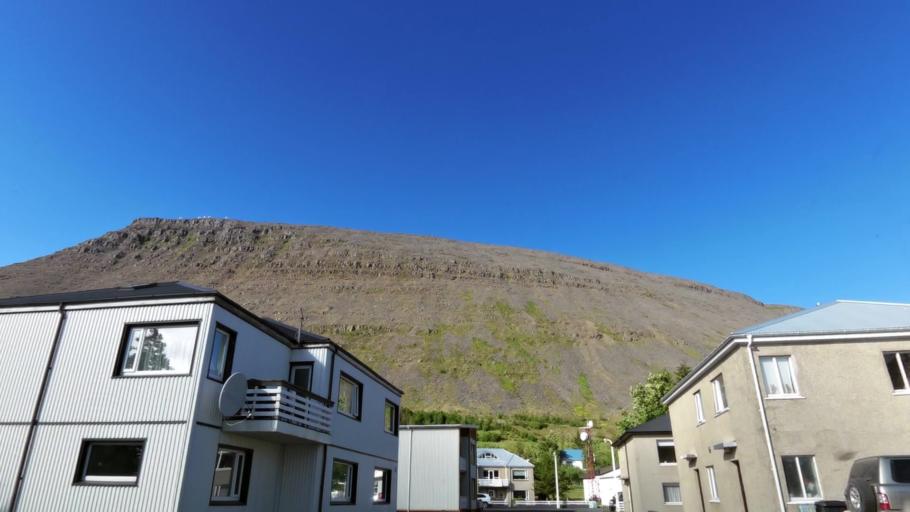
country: IS
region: West
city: Olafsvik
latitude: 65.5975
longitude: -23.9990
